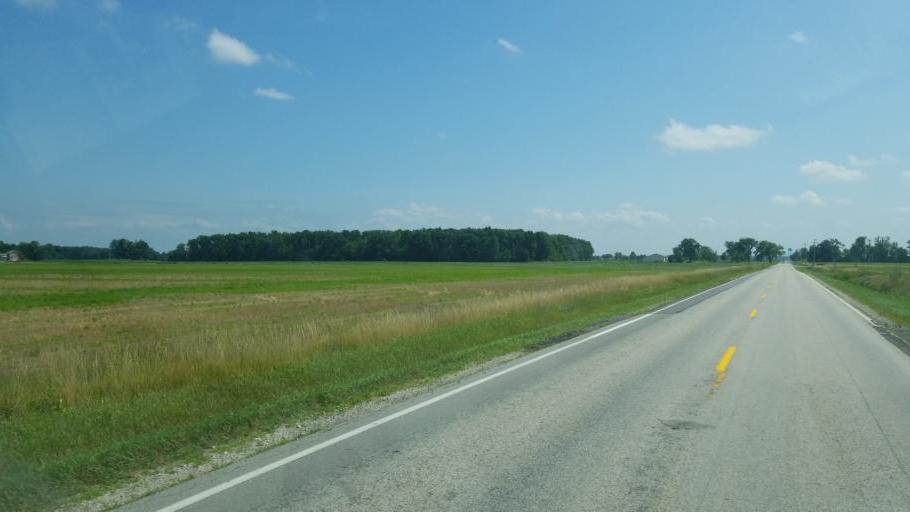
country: US
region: Ohio
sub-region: Huron County
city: Bellevue
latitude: 41.1925
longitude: -82.8375
